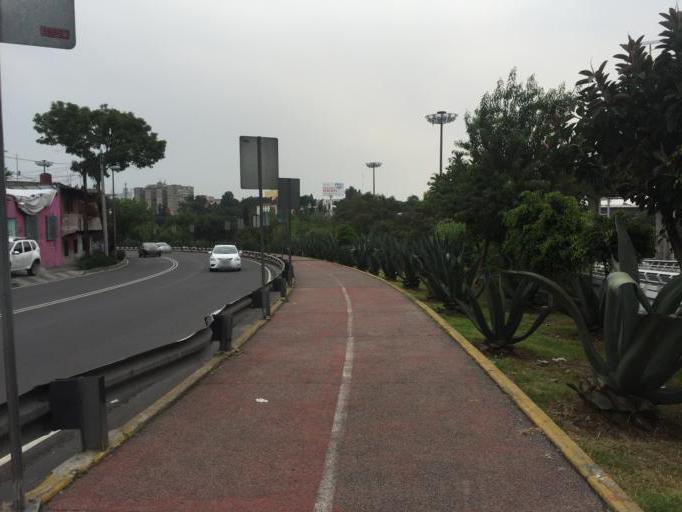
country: MX
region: Mexico City
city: Polanco
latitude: 19.3992
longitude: -99.1908
